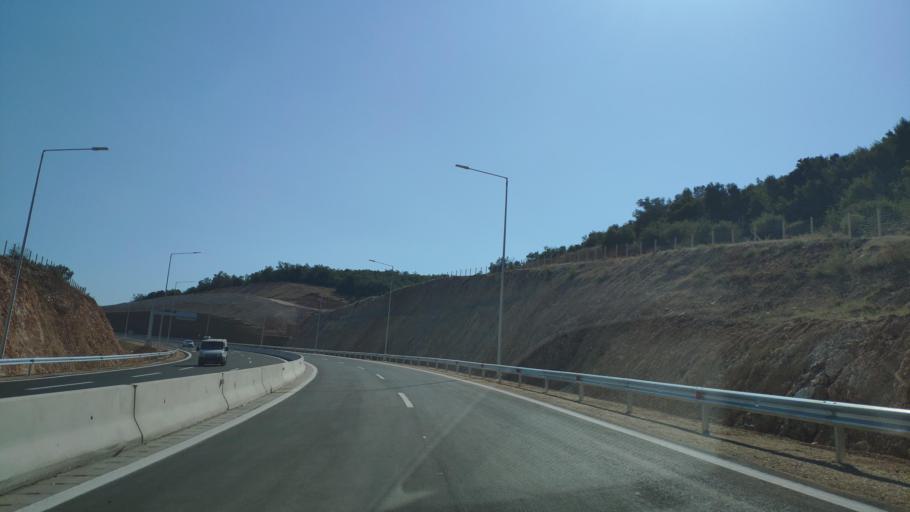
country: GR
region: West Greece
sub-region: Nomos Aitolias kai Akarnanias
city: Stanos
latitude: 38.7781
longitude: 21.1838
